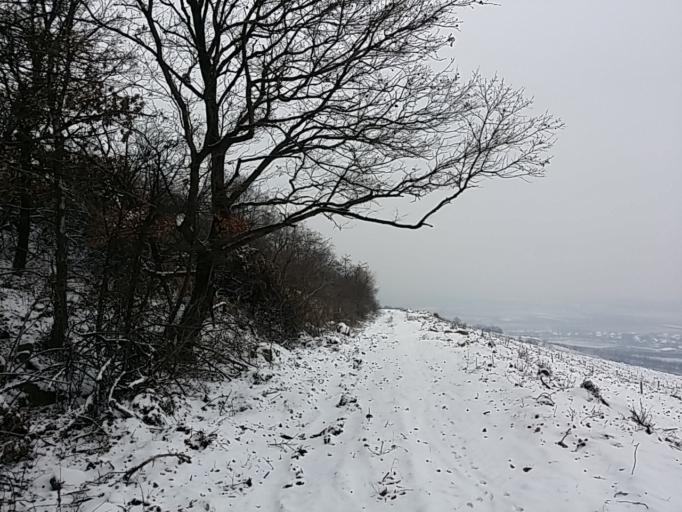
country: HU
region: Heves
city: Abasar
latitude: 47.8032
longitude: 19.9899
